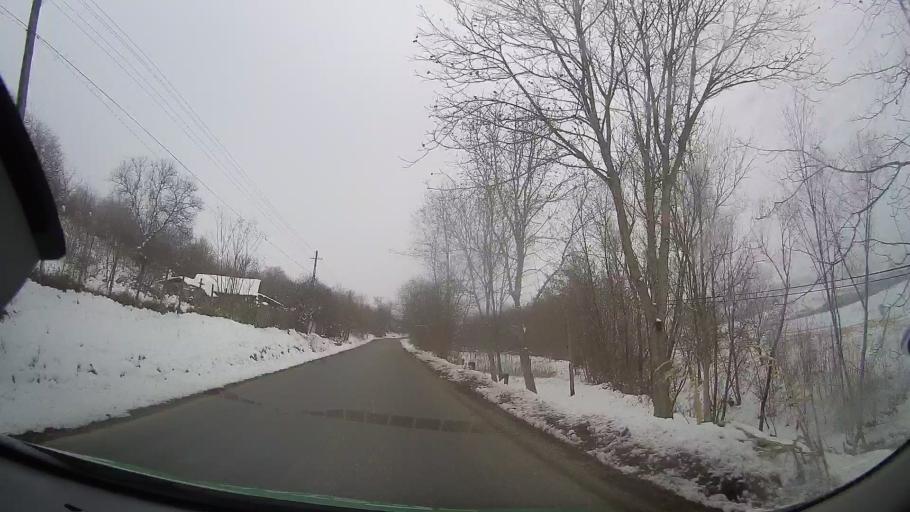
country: RO
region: Bacau
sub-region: Comuna Vultureni
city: Vultureni
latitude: 46.3866
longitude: 27.2781
